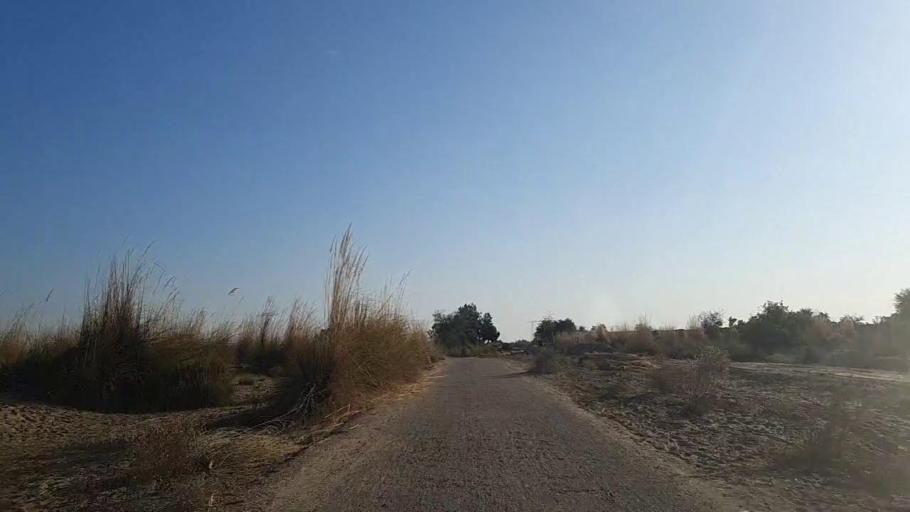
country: PK
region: Sindh
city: Khadro
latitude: 26.2760
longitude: 68.8603
